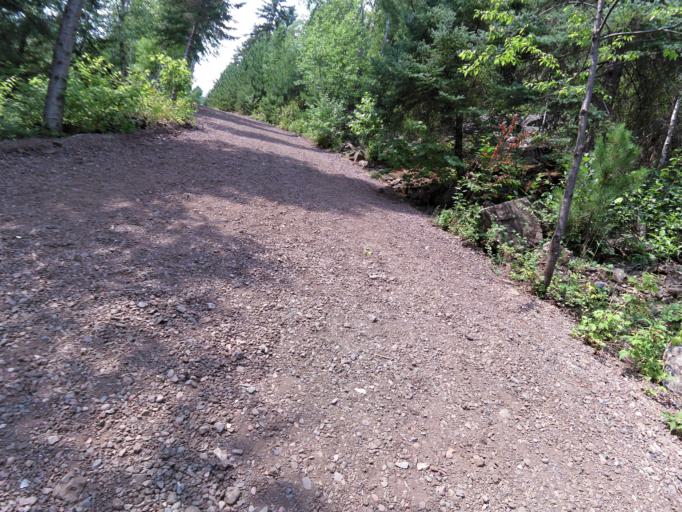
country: CA
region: Ontario
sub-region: Thunder Bay District
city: Thunder Bay
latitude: 48.7978
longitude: -88.6163
